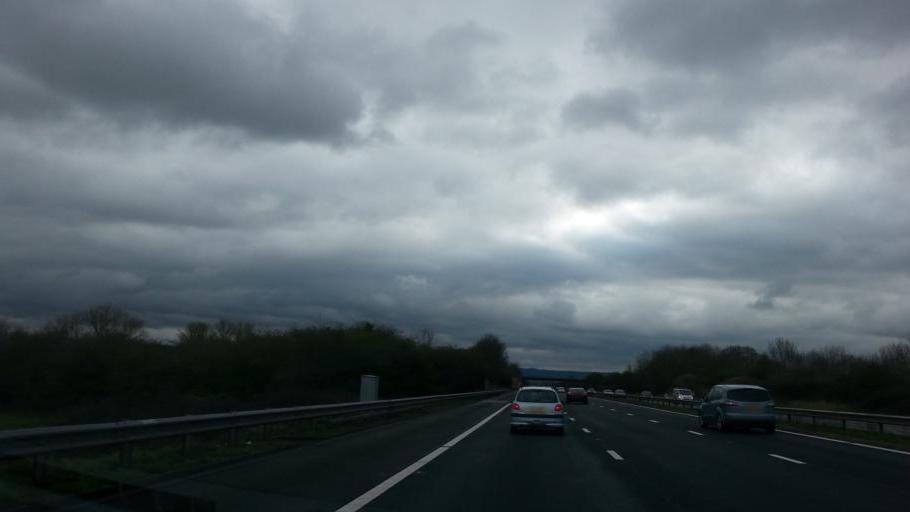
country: GB
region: England
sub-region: Somerset
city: Creech Saint Michael
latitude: 51.0336
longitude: -3.0441
